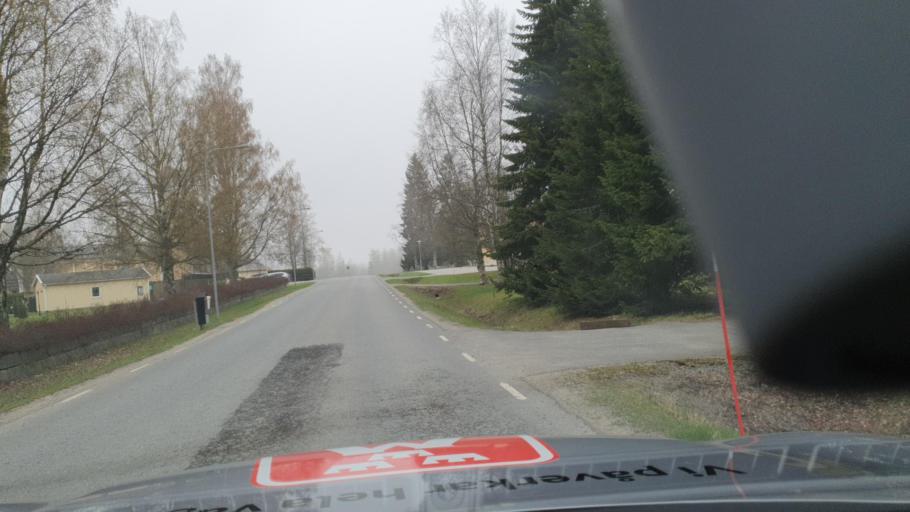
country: SE
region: Vaesternorrland
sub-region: OErnskoeldsviks Kommun
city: Husum
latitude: 63.4818
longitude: 18.9749
